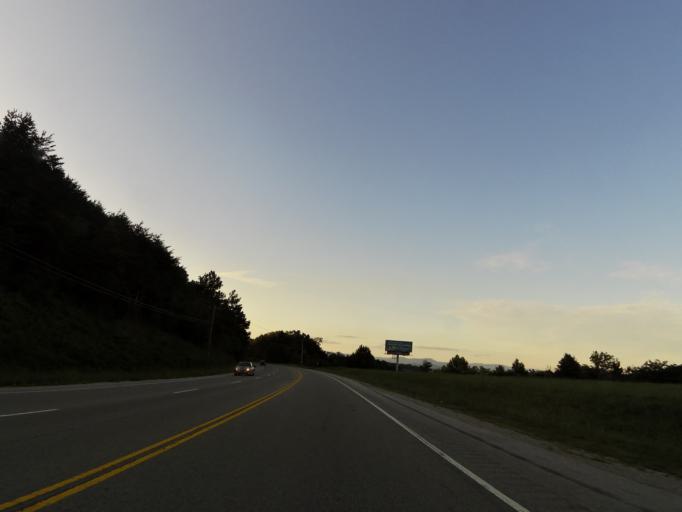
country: US
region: Tennessee
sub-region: Roane County
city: Midtown
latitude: 35.8376
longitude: -84.5425
